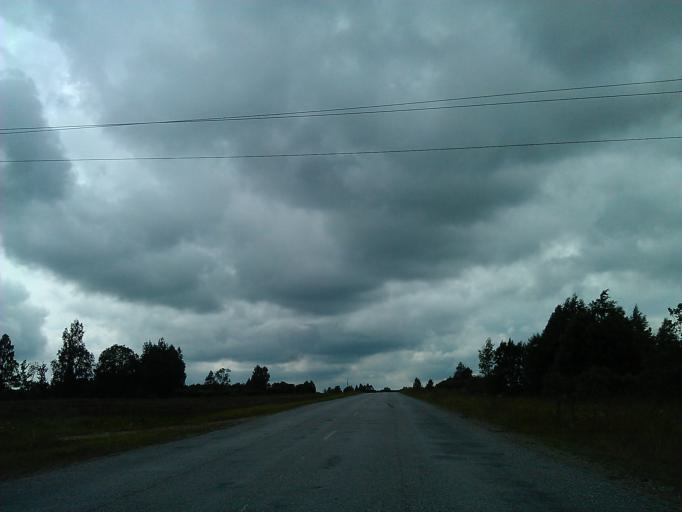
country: LV
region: Aizpute
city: Aizpute
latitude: 56.7991
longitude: 21.6772
